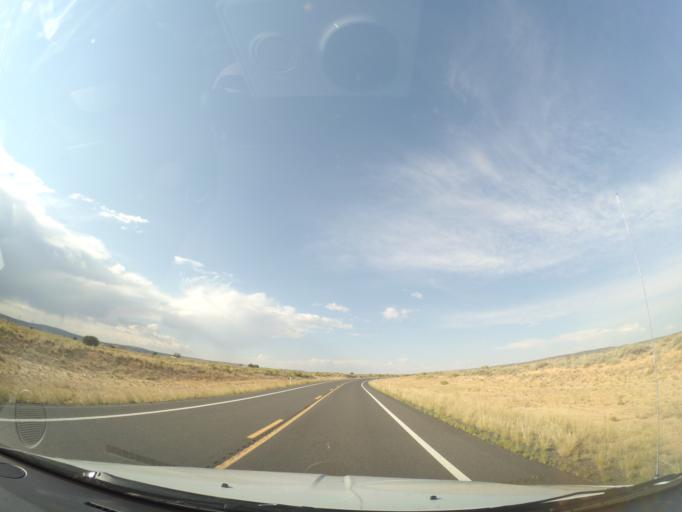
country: US
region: Arizona
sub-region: Coconino County
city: Tuba City
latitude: 36.4551
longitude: -111.4242
